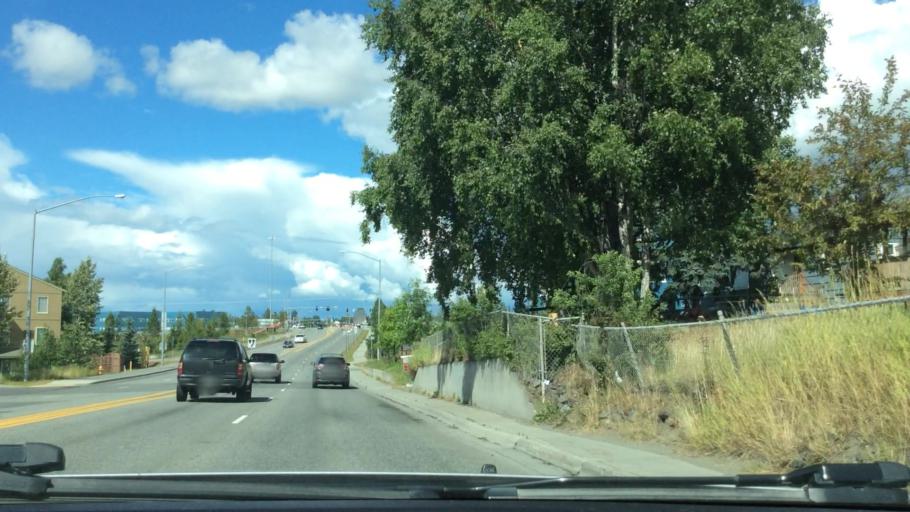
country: US
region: Alaska
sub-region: Anchorage Municipality
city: Anchorage
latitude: 61.2178
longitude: -149.8083
